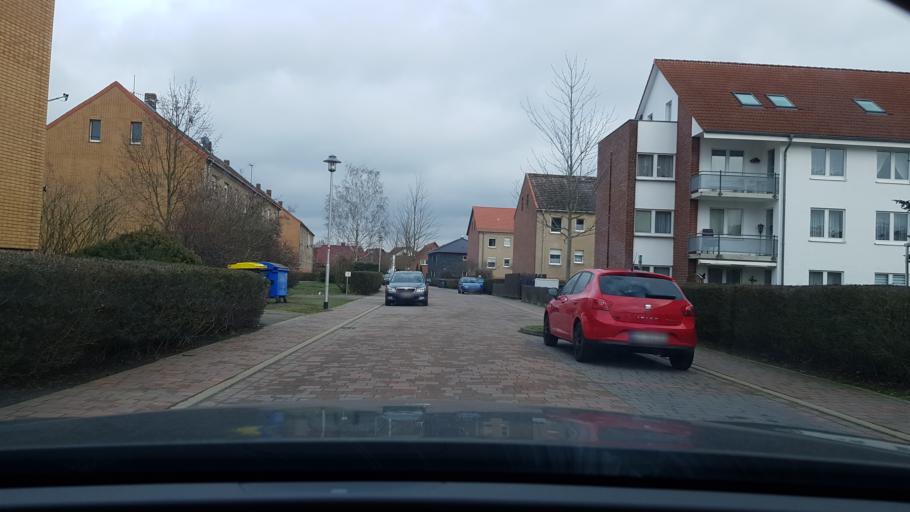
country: DE
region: Saxony-Anhalt
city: Oebisfelde
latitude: 52.4309
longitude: 10.9962
